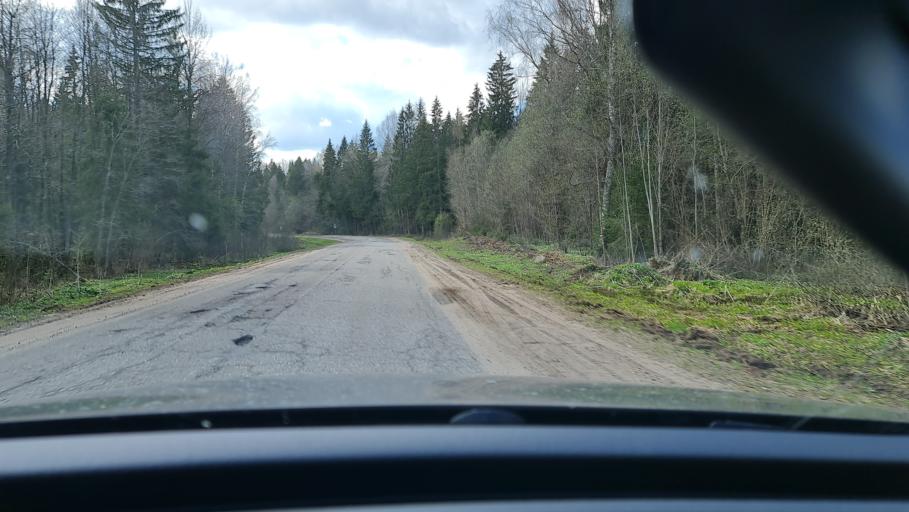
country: RU
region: Tverskaya
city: Toropets
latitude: 56.6268
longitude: 31.4338
